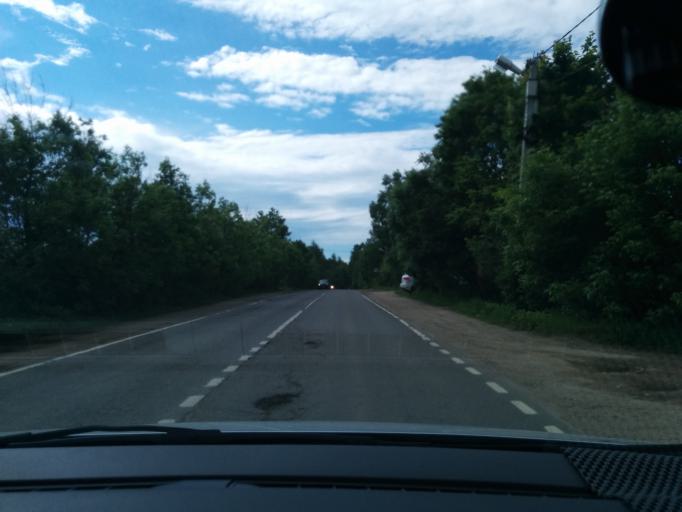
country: RU
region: Moskovskaya
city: Lugovaya
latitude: 56.0511
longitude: 37.4861
